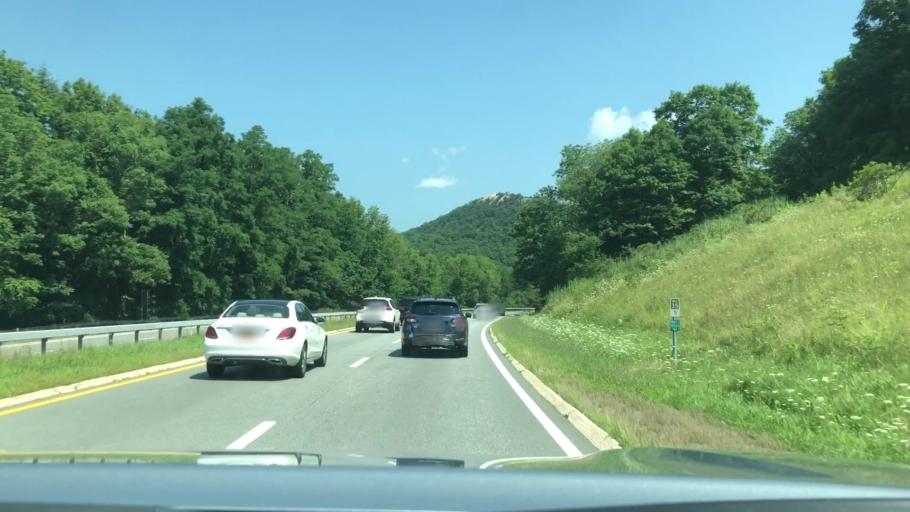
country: US
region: New York
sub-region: Orange County
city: Fort Montgomery
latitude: 41.3180
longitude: -74.0153
